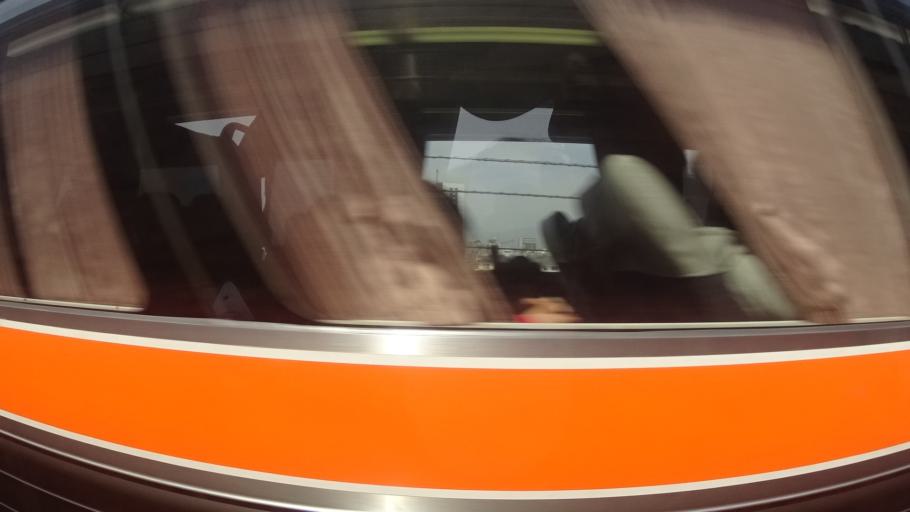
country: JP
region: Mie
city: Suzuka
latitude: 34.8802
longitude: 136.5896
